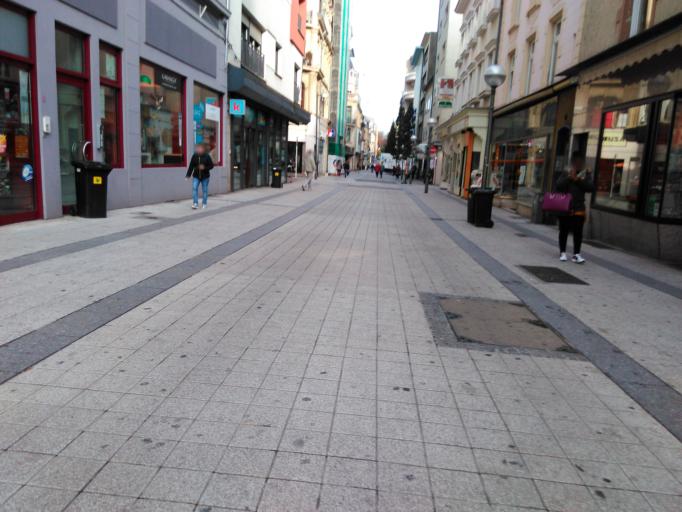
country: LU
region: Luxembourg
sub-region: Canton d'Esch-sur-Alzette
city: Esch-sur-Alzette
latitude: 49.4938
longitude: 5.9834
